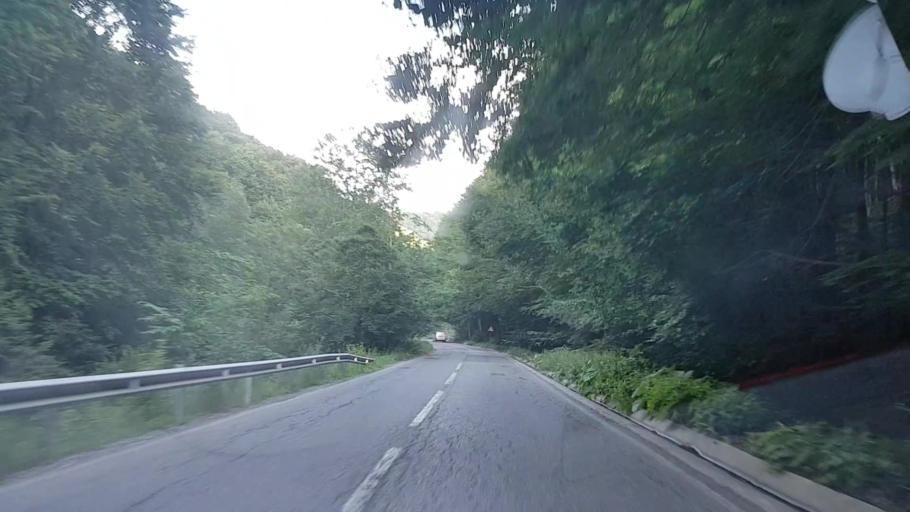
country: RO
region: Harghita
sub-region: Comuna Praid
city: Ocna de Sus
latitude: 46.5967
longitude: 25.2401
